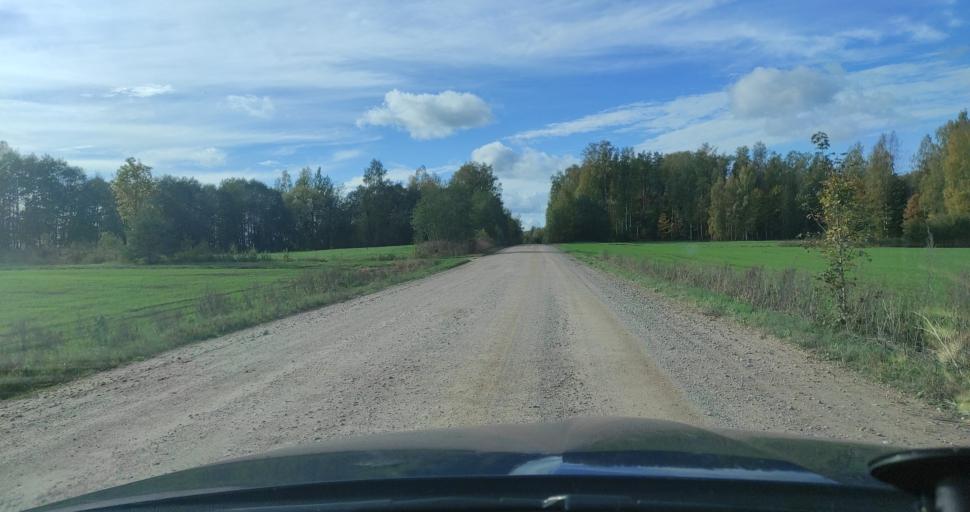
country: LV
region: Jaunpils
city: Jaunpils
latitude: 56.8303
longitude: 22.9801
